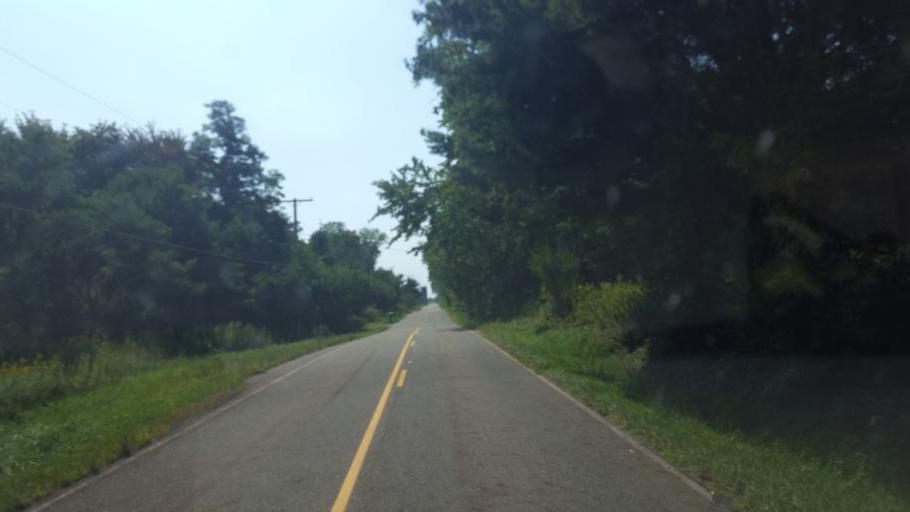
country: US
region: Ohio
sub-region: Lake County
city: Madison
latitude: 41.6825
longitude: -81.0377
